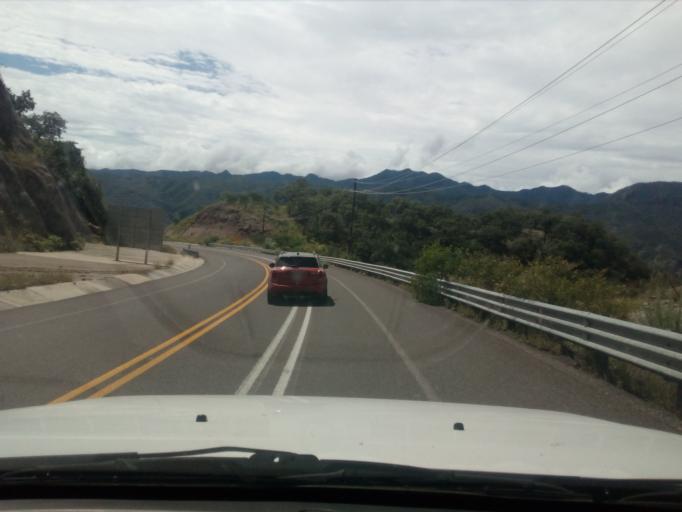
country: MX
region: Durango
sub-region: Pueblo Nuevo
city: La Ciudad
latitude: 23.5610
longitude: -105.7514
